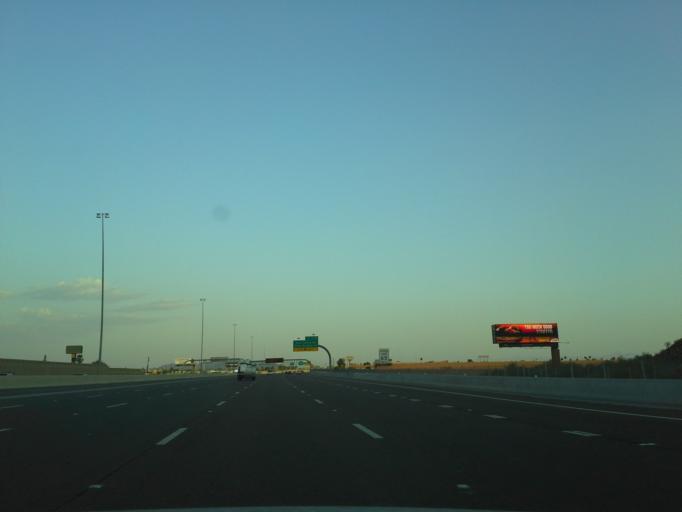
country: US
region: Arizona
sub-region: Maricopa County
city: Peoria
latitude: 33.6942
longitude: -112.1138
